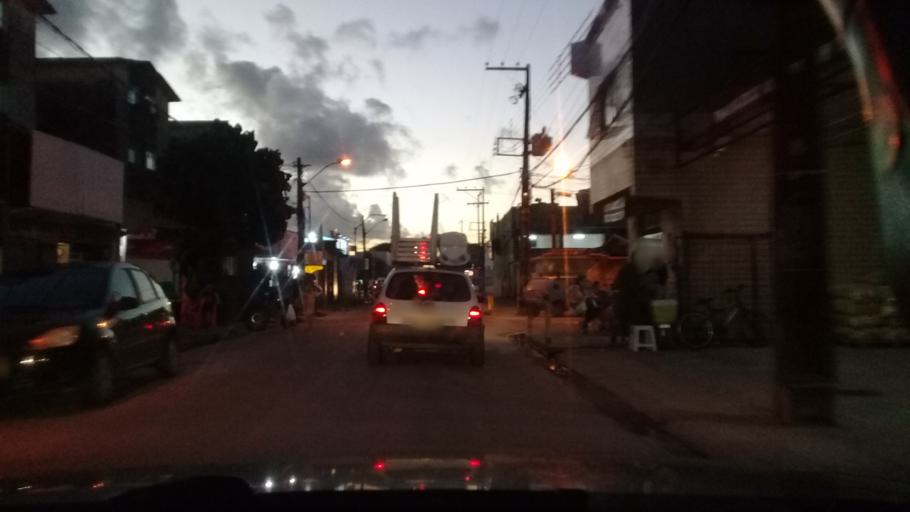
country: BR
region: Pernambuco
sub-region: Recife
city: Recife
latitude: -8.1118
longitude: -34.9192
